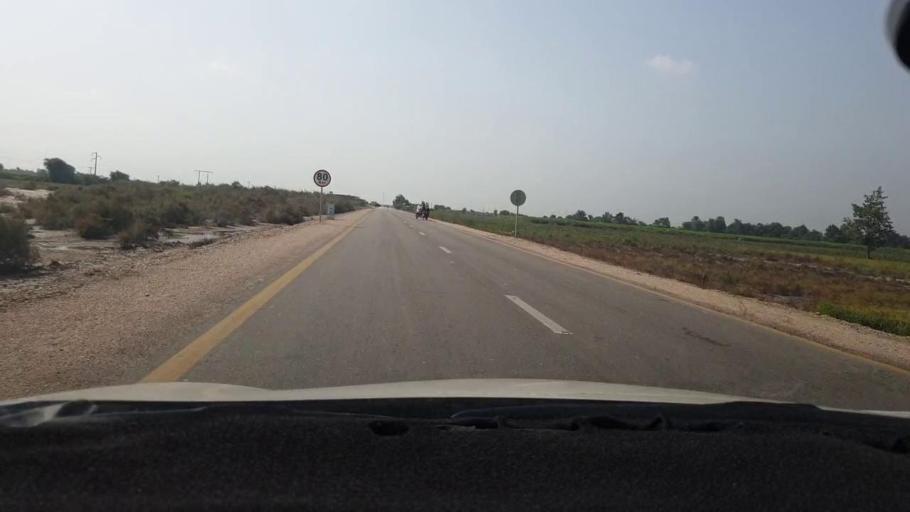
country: PK
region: Sindh
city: Jhol
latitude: 25.8527
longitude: 69.0604
